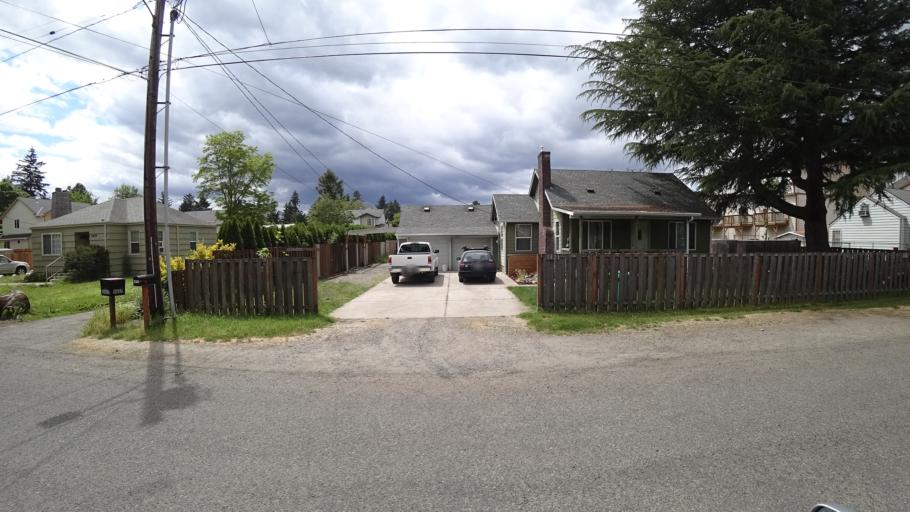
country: US
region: Oregon
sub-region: Clackamas County
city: Happy Valley
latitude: 45.4976
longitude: -122.5164
